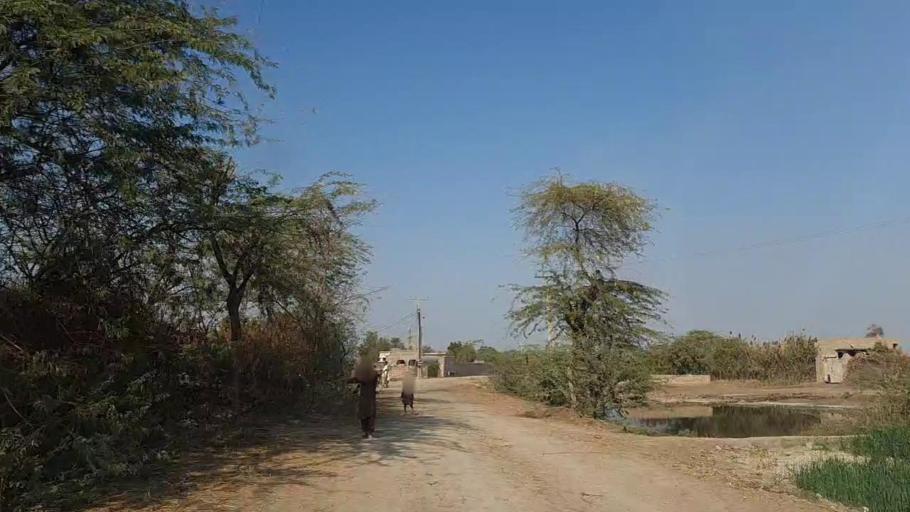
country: PK
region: Sindh
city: Daur
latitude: 26.4618
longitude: 68.3032
